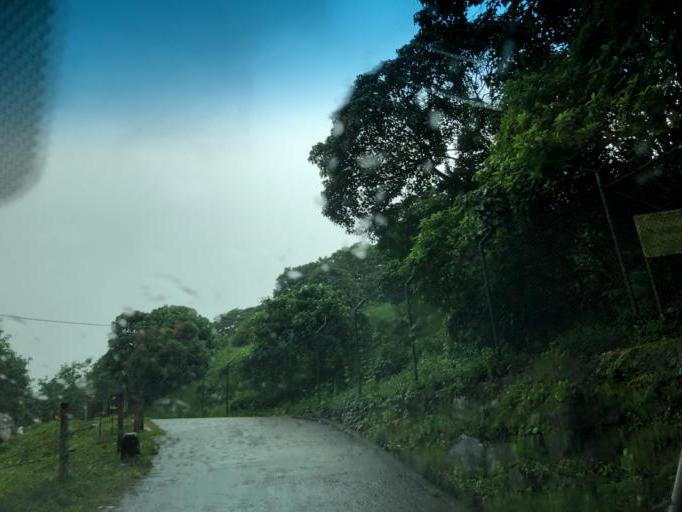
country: LK
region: Western
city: Horana South
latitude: 6.7204
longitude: 80.0617
